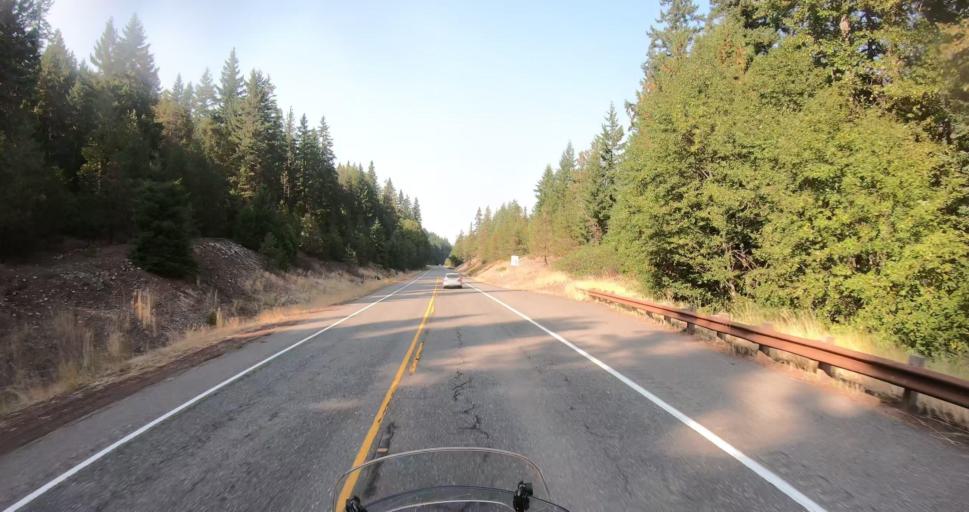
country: US
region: Oregon
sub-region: Hood River County
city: Odell
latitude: 45.4302
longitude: -121.5751
